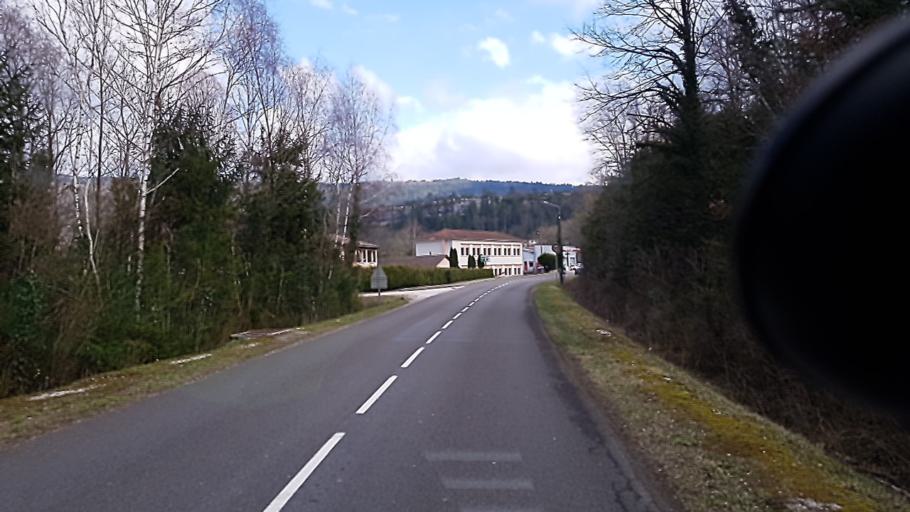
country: FR
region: Rhone-Alpes
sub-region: Departement de l'Ain
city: Dortan
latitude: 46.3225
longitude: 5.6544
